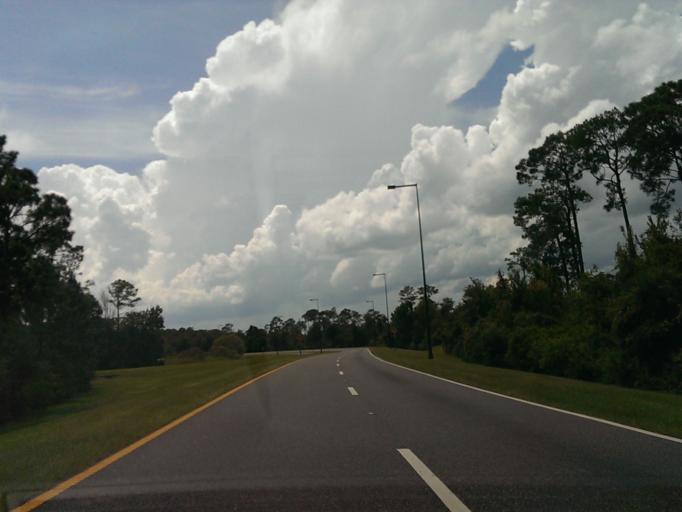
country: US
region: Florida
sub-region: Osceola County
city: Celebration
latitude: 28.3826
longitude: -81.5571
